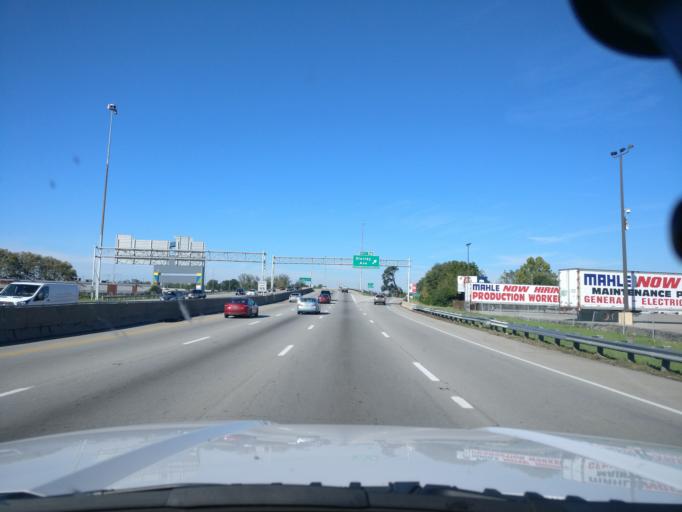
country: US
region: Ohio
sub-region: Montgomery County
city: Northridge
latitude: 39.7855
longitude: -84.1844
